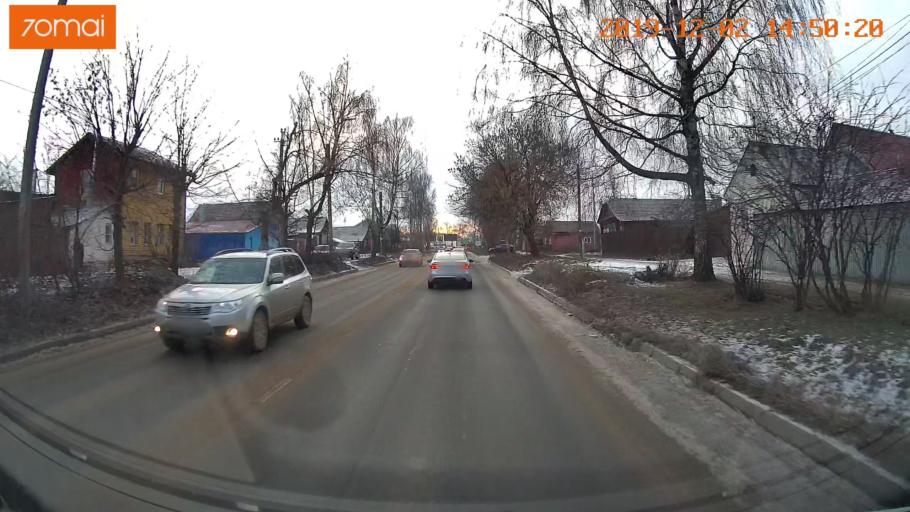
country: RU
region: Ivanovo
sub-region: Gorod Ivanovo
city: Ivanovo
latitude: 56.9806
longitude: 41.0060
